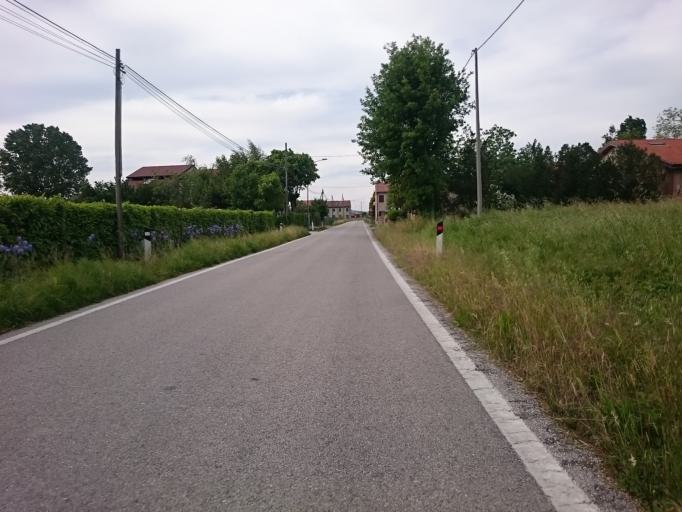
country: IT
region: Veneto
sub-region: Provincia di Padova
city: Granze
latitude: 45.1657
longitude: 11.7218
